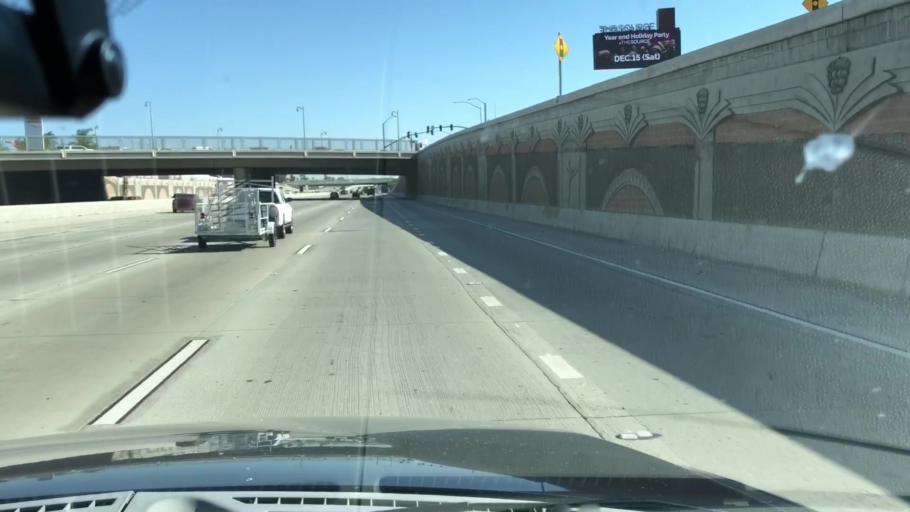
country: US
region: California
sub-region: Orange County
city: Buena Park
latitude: 33.8669
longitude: -117.9996
